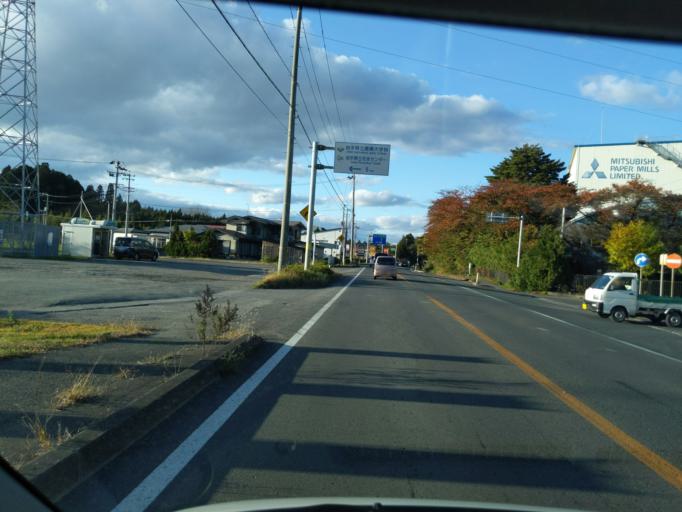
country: JP
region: Iwate
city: Kitakami
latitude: 39.2293
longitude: 141.0927
